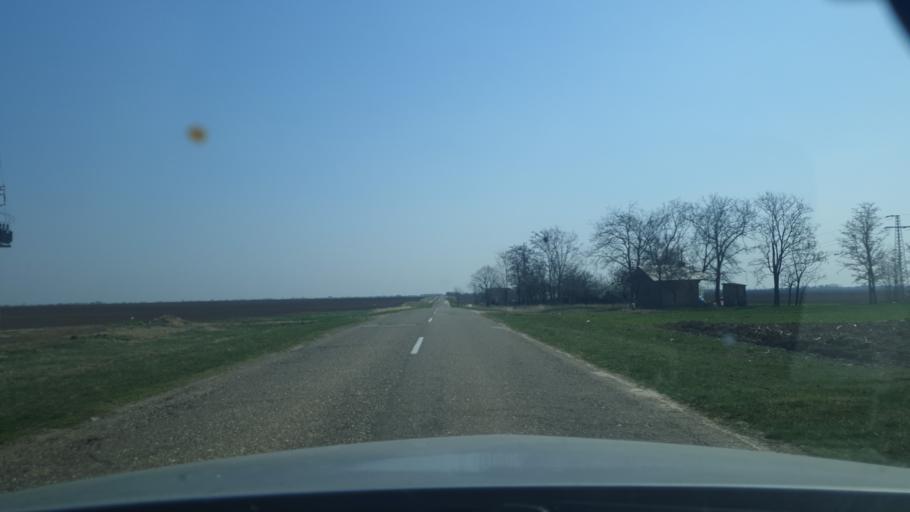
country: RS
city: Sasinci
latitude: 45.0331
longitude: 19.7465
